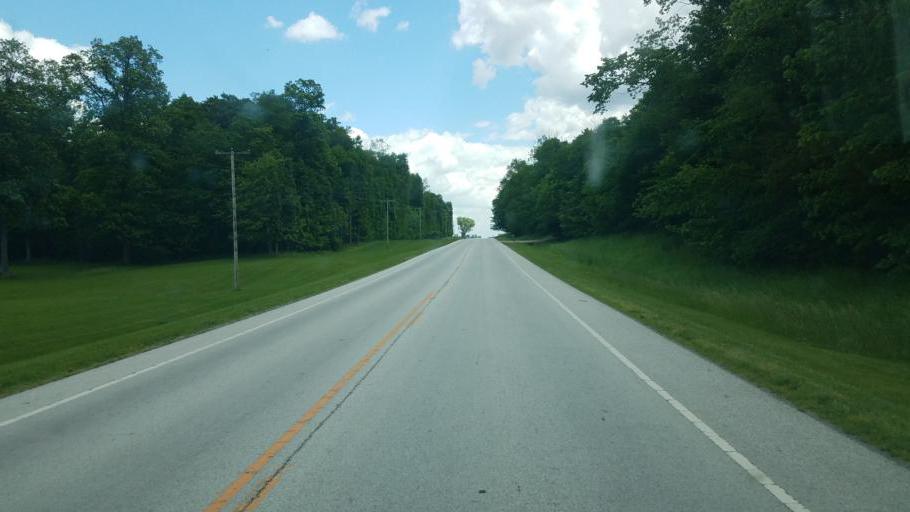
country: US
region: Ohio
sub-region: Wyandot County
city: Upper Sandusky
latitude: 40.8407
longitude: -83.1456
